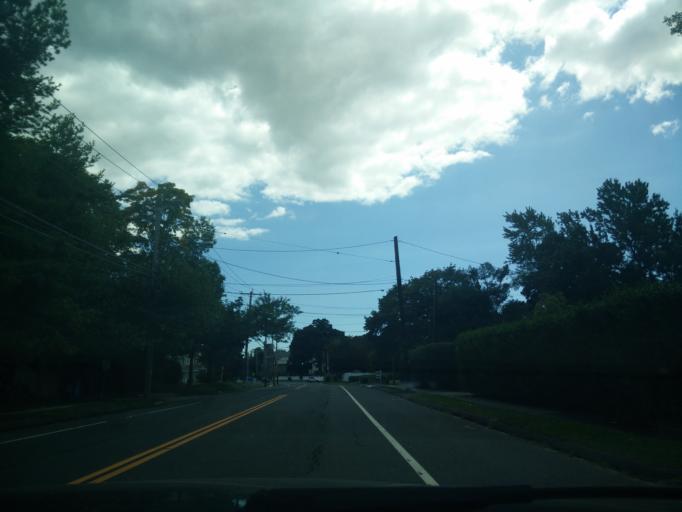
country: US
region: Connecticut
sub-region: Fairfield County
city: Bridgeport
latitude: 41.1948
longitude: -73.2298
